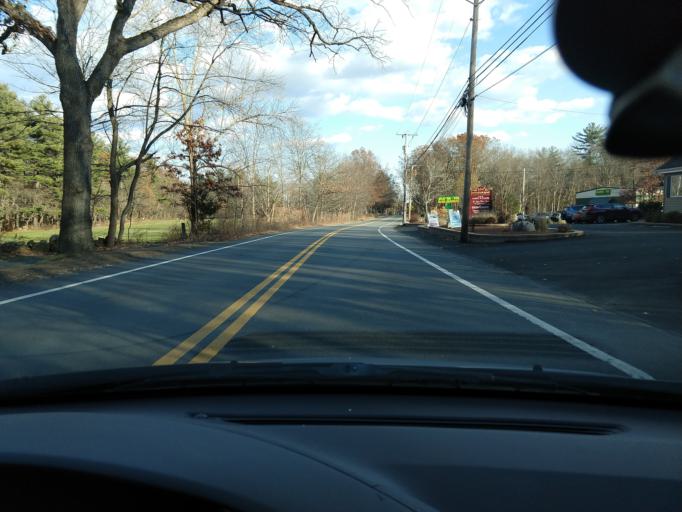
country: US
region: Massachusetts
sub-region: Middlesex County
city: Littleton Common
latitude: 42.5502
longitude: -71.4646
